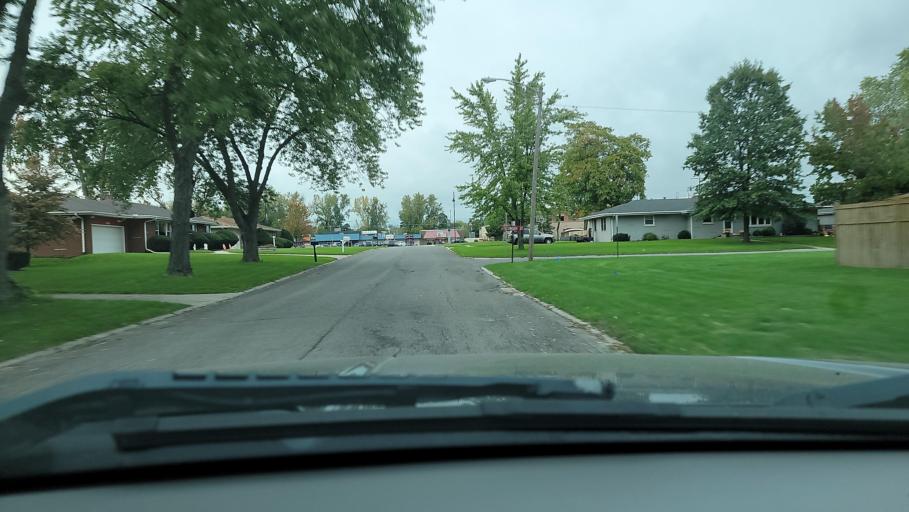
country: US
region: Indiana
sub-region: Porter County
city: Portage
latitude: 41.5745
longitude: -87.1739
